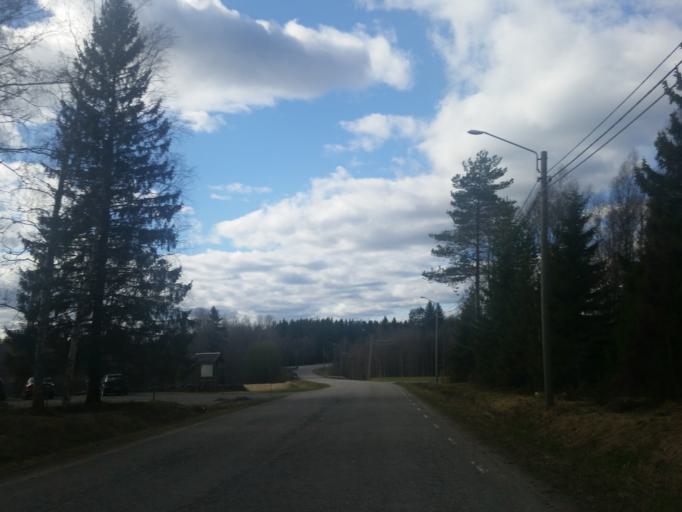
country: SE
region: Vaesterbotten
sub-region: Robertsfors Kommun
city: Robertsfors
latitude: 64.0454
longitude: 20.8574
